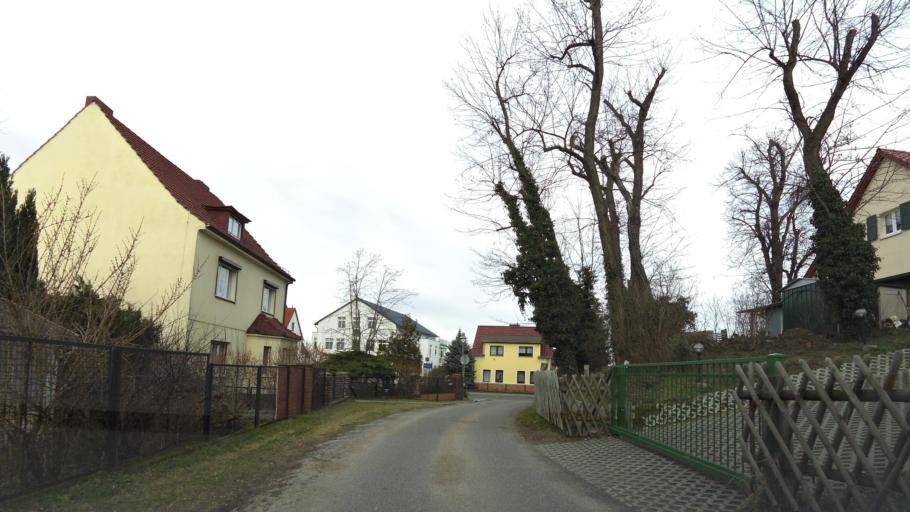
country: DE
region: Brandenburg
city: Michendorf
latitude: 52.3507
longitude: 13.0114
